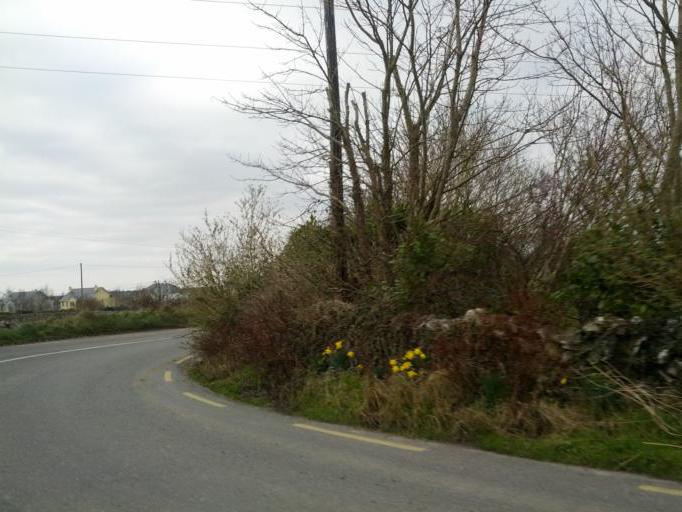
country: IE
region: Connaught
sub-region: County Galway
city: Oranmore
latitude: 53.2090
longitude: -8.8345
